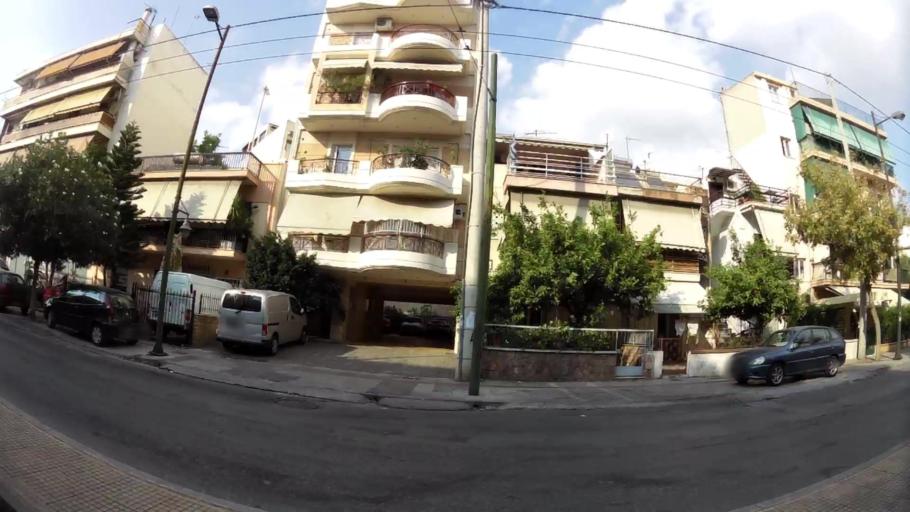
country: GR
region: Attica
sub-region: Nomarchia Athinas
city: Kallithea
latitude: 37.9445
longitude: 23.6935
